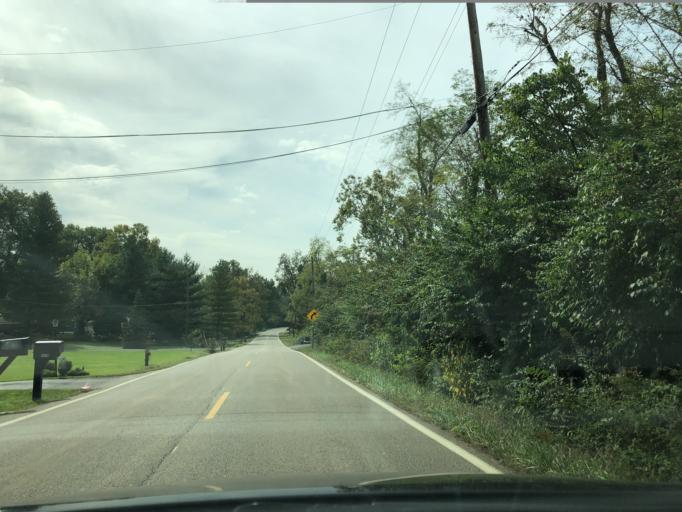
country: US
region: Ohio
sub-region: Hamilton County
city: The Village of Indian Hill
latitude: 39.2371
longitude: -84.2888
